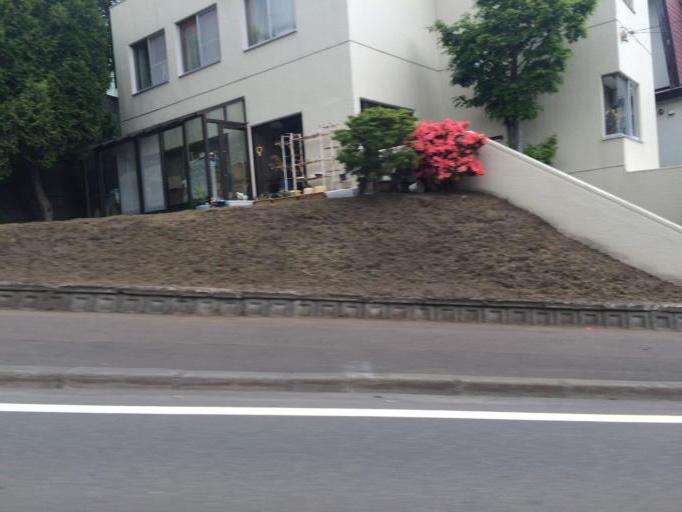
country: JP
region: Hokkaido
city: Sapporo
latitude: 43.0419
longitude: 141.2909
